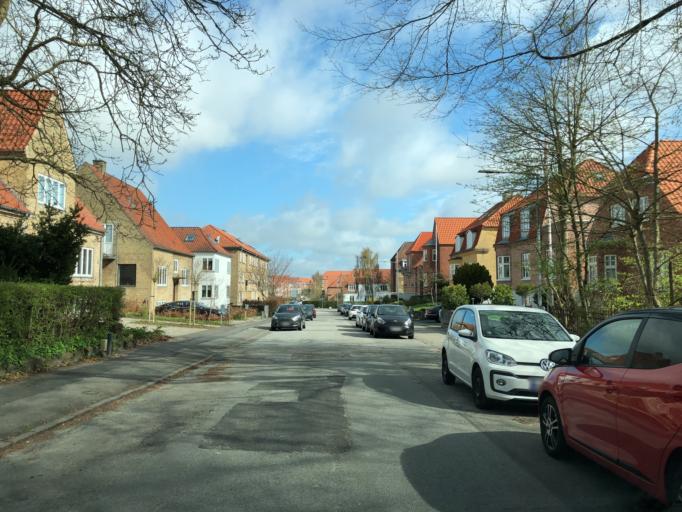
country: DK
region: North Denmark
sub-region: Alborg Kommune
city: Aalborg
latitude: 57.0491
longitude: 9.9001
